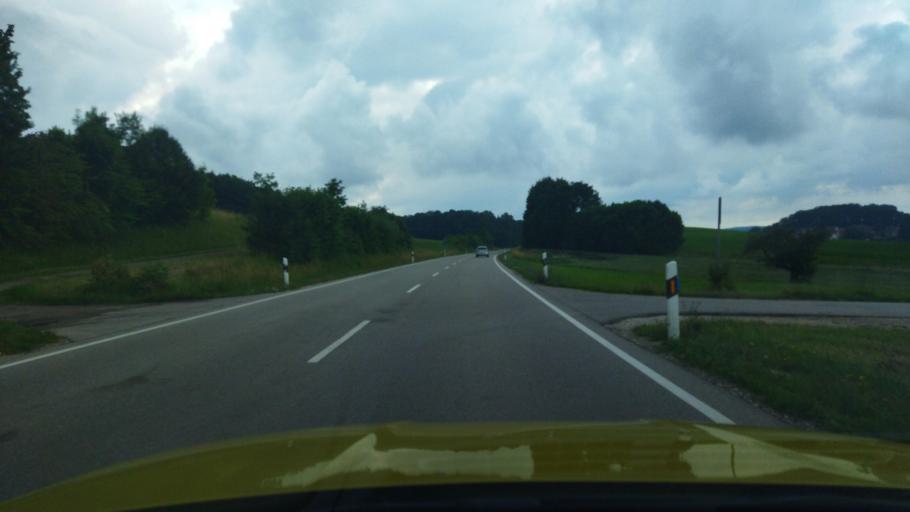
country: DE
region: Bavaria
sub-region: Regierungsbezirk Mittelfranken
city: Pfofeld
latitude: 49.1146
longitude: 10.8560
